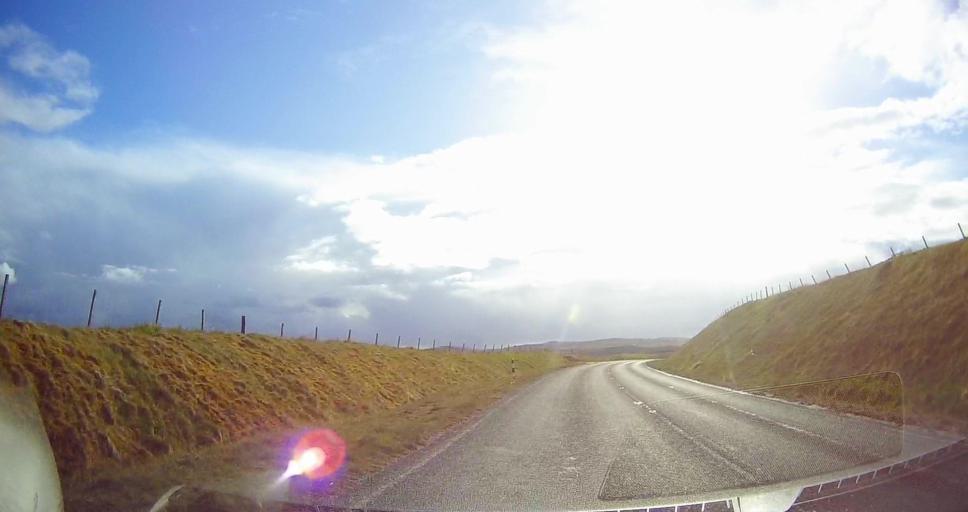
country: GB
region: Scotland
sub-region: Shetland Islands
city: Lerwick
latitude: 60.3706
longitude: -1.3251
